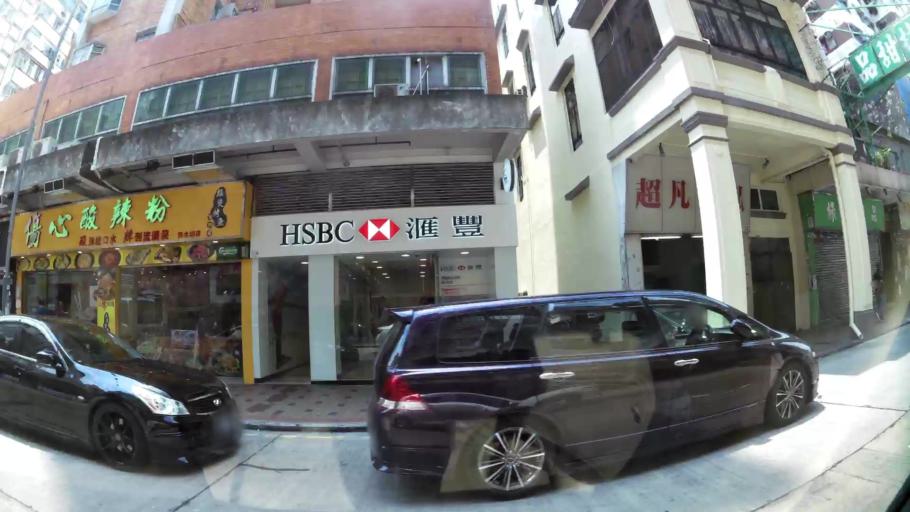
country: HK
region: Sham Shui Po
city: Sham Shui Po
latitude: 22.3326
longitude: 114.1630
